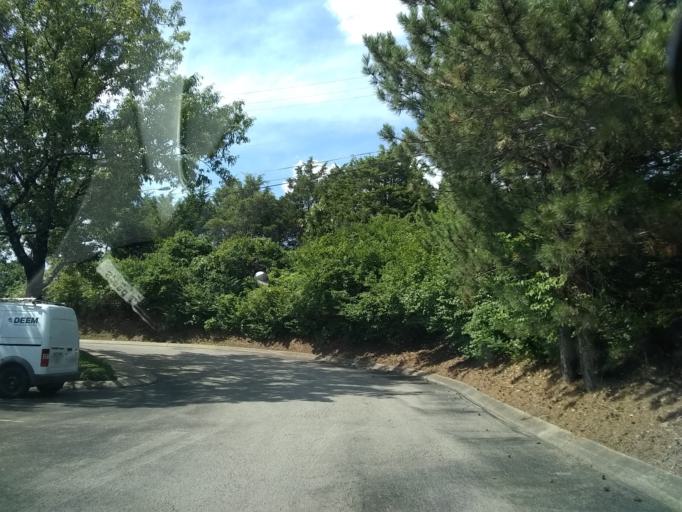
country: US
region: Tennessee
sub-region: Davidson County
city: Nashville
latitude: 36.1470
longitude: -86.7011
